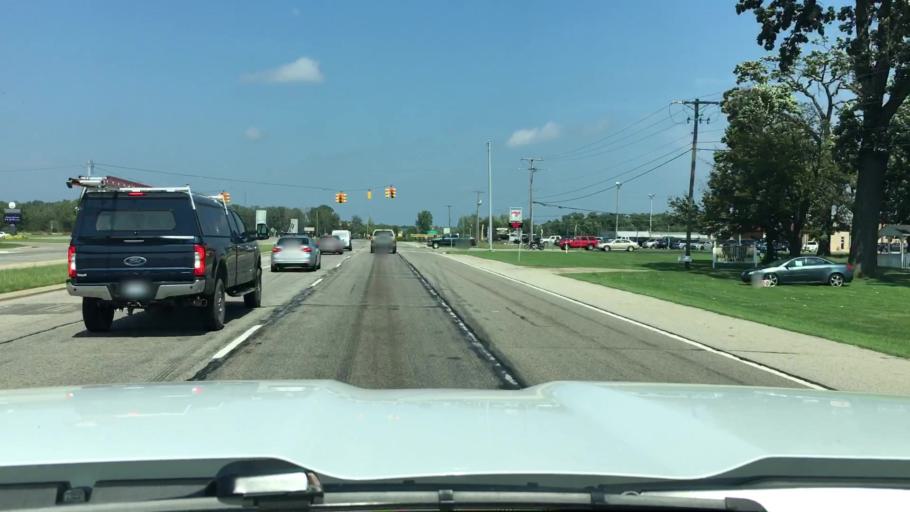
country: US
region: Michigan
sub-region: Kalamazoo County
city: Schoolcraft
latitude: 42.1425
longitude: -85.6376
